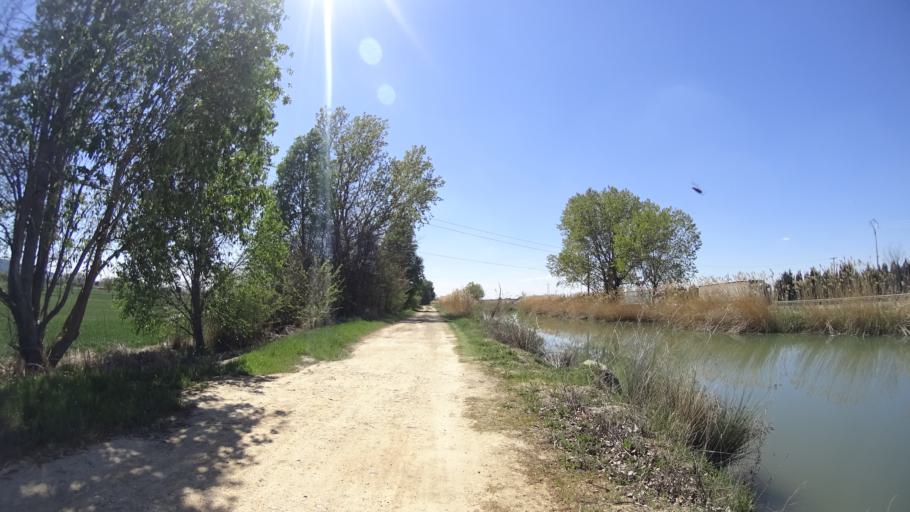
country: ES
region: Castille and Leon
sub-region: Provincia de Valladolid
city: Cabezon
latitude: 41.7460
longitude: -4.6541
